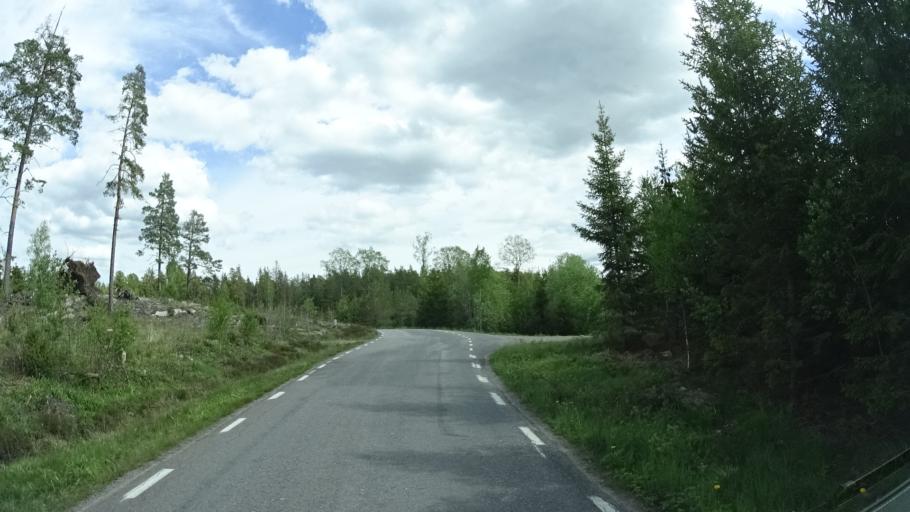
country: SE
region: OEstergoetland
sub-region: Finspangs Kommun
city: Finspang
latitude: 58.6097
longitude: 15.7244
